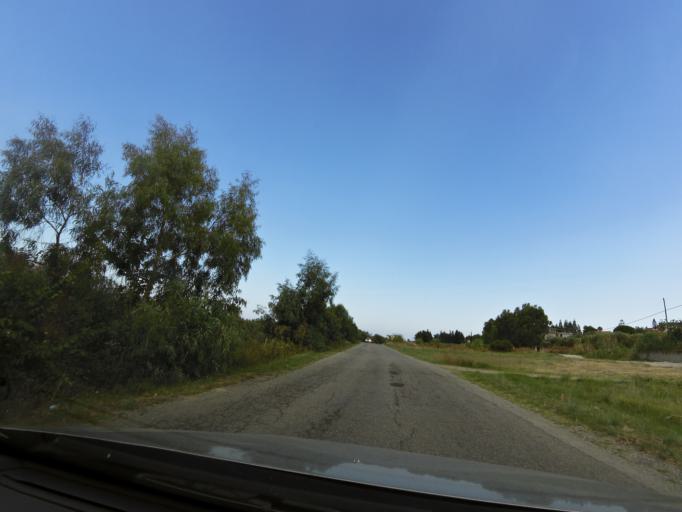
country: IT
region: Calabria
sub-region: Provincia di Reggio Calabria
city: Monasterace Marina
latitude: 38.4218
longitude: 16.5539
